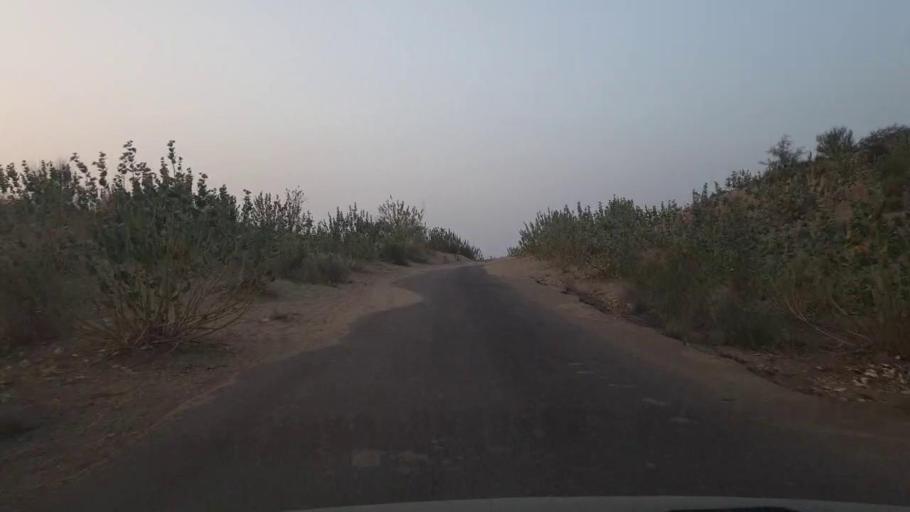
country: PK
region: Sindh
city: Umarkot
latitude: 25.3130
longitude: 70.0602
